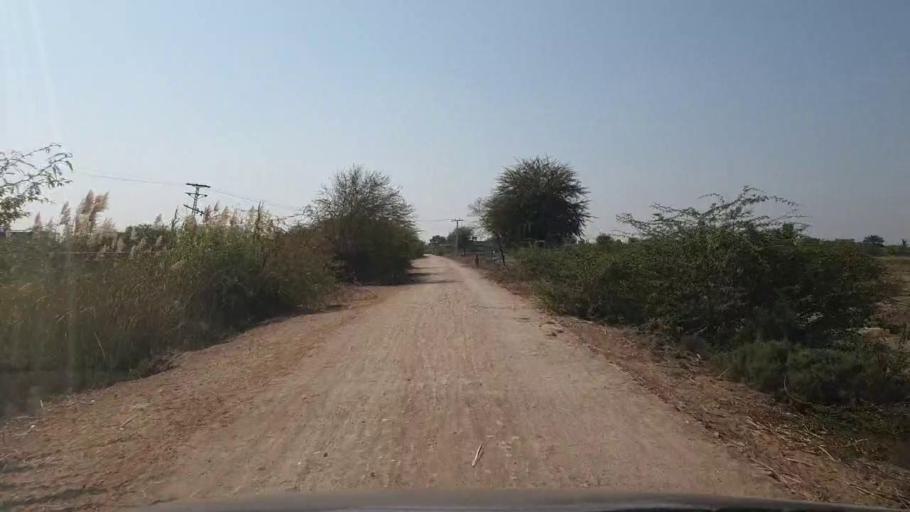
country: PK
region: Sindh
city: Samaro
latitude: 25.2514
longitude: 69.2769
